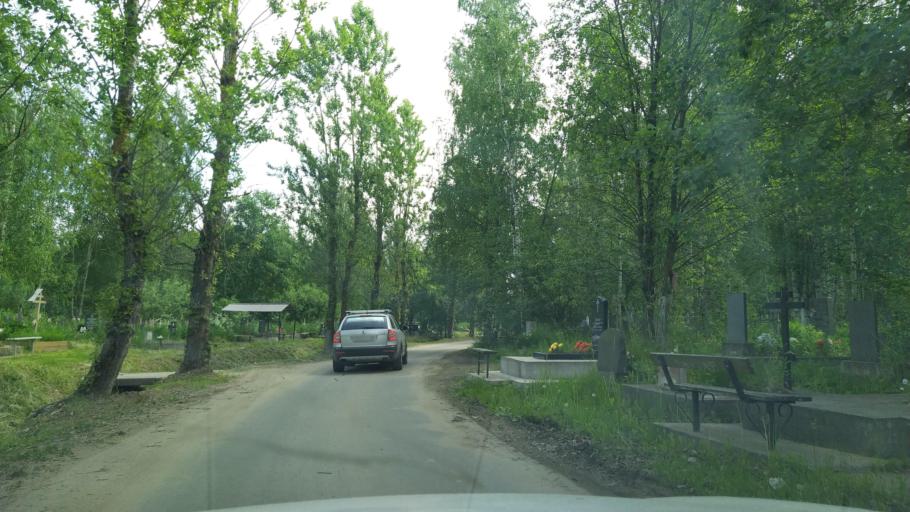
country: RU
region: St.-Petersburg
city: Dachnoye
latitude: 59.7715
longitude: 30.2660
